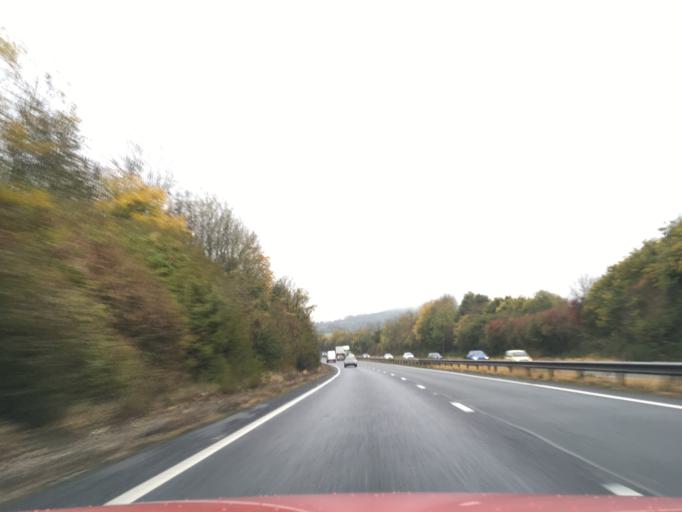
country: GB
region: England
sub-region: Hampshire
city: Highclere
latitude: 51.3276
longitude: -1.3461
